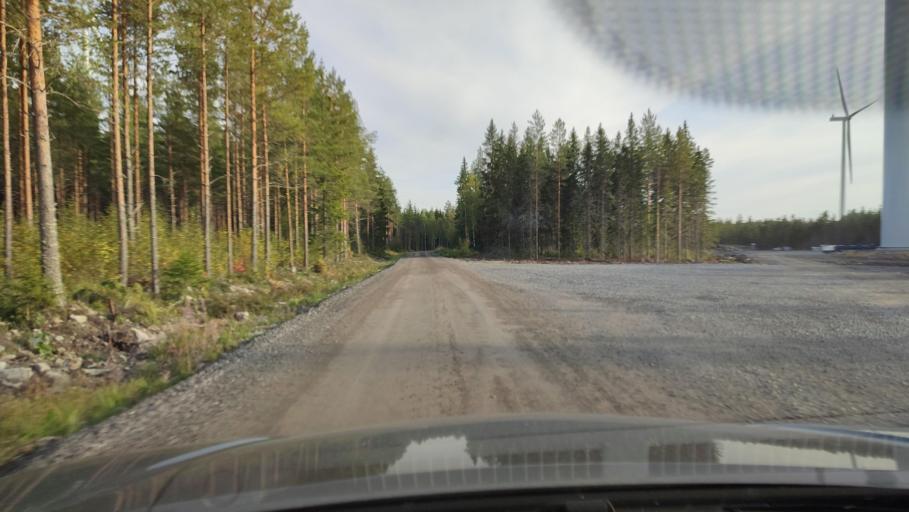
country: FI
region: Southern Ostrobothnia
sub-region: Suupohja
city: Karijoki
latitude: 62.1617
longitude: 21.6107
